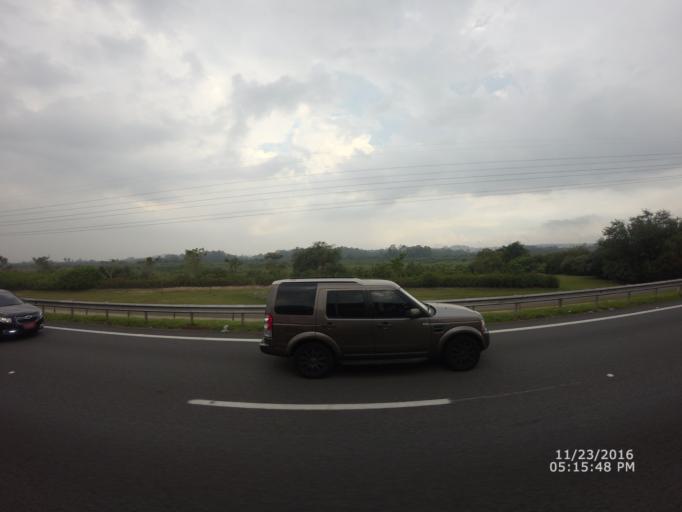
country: BR
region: Sao Paulo
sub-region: Guarulhos
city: Guarulhos
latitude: -23.4836
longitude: -46.5271
